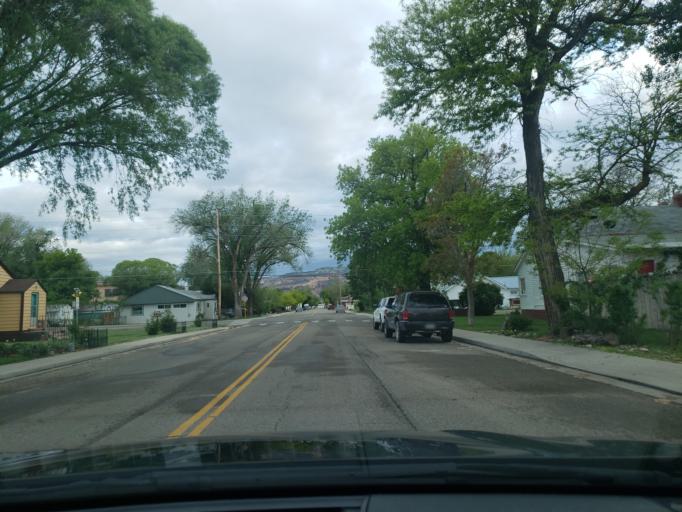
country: US
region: Colorado
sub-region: Mesa County
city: Fruita
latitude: 39.1612
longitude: -108.7314
